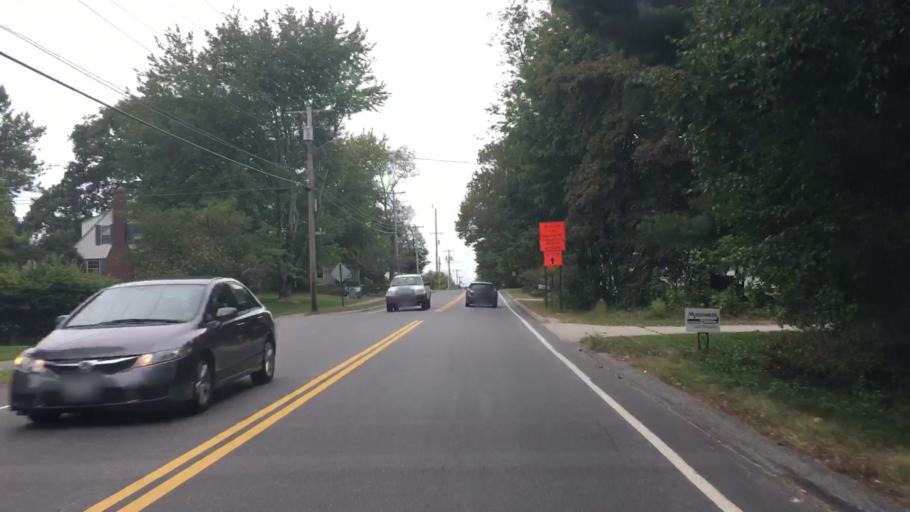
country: US
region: Maine
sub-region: Cumberland County
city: Yarmouth
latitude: 43.8076
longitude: -70.1744
